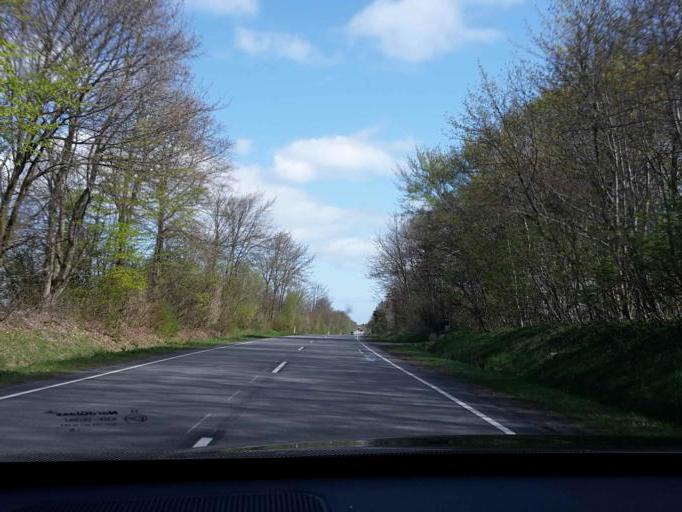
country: DK
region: South Denmark
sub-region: Vejen Kommune
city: Holsted
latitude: 55.6236
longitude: 8.9445
